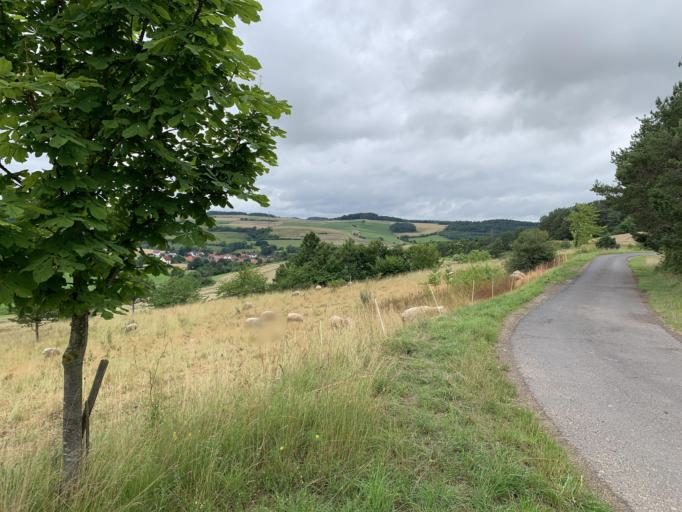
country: DE
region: Hesse
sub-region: Regierungsbezirk Kassel
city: Ronshausen
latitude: 50.9732
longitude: 9.8829
